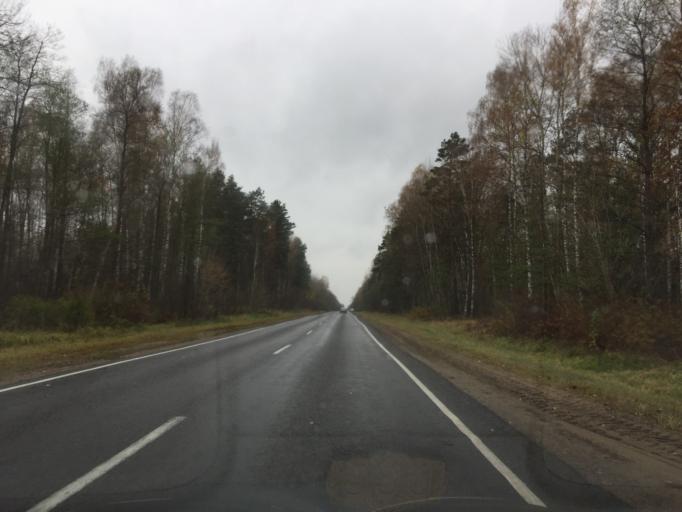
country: BY
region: Mogilev
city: Slawharad
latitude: 53.3599
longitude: 30.8406
